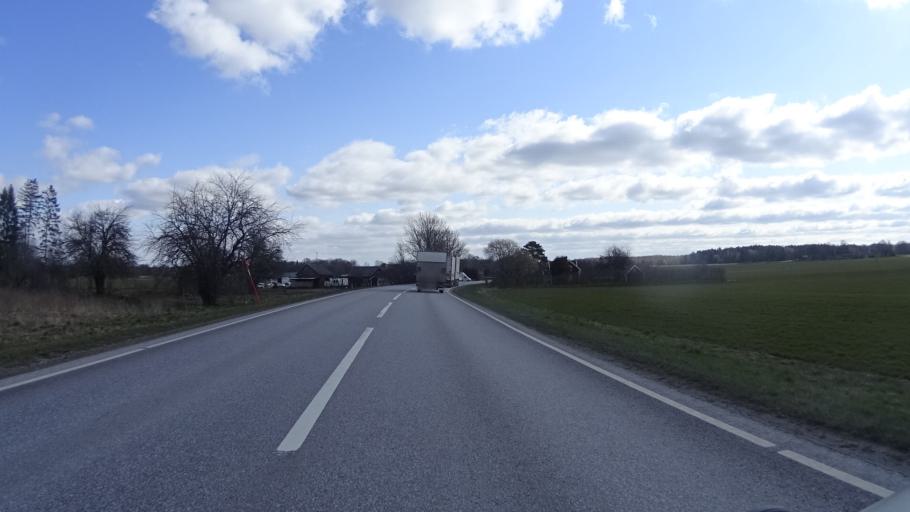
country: SE
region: OEstergoetland
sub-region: Mjolby Kommun
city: Mantorp
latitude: 58.3781
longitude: 15.2559
